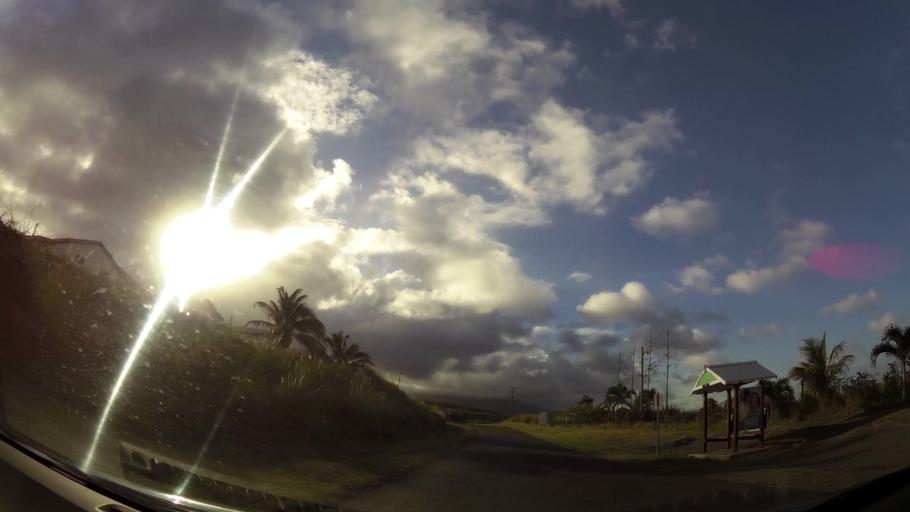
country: KN
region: Saint Mary Cayon
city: Cayon
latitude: 17.3458
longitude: -62.7189
